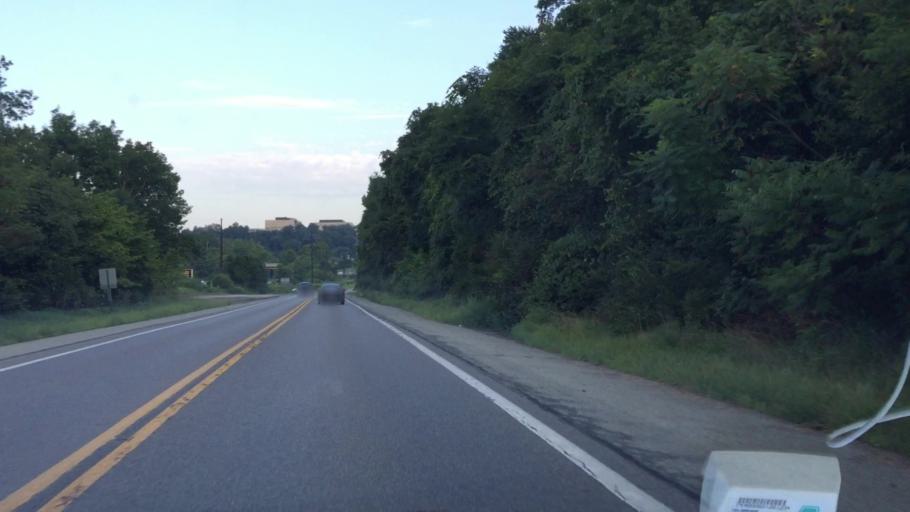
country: US
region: Pennsylvania
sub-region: Allegheny County
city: Enlow
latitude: 40.4566
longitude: -80.1809
